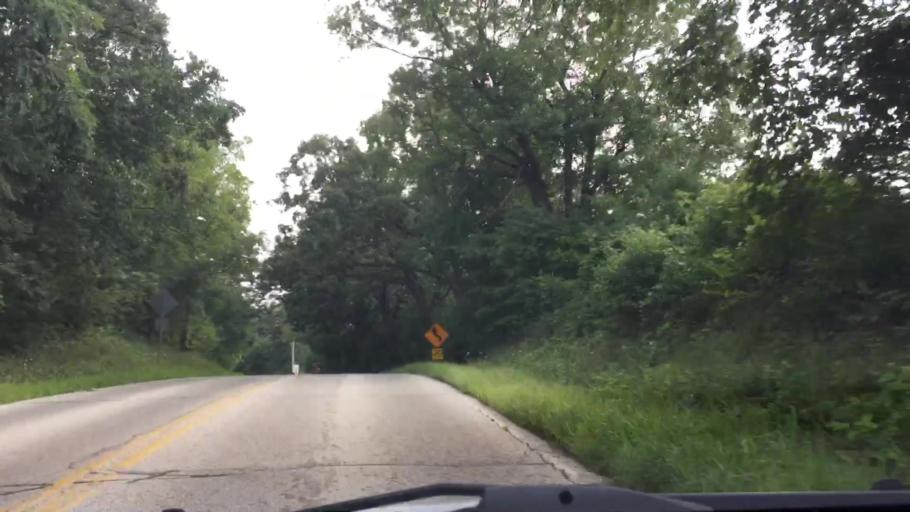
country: US
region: Wisconsin
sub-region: Waukesha County
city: Wales
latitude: 43.0295
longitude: -88.3653
